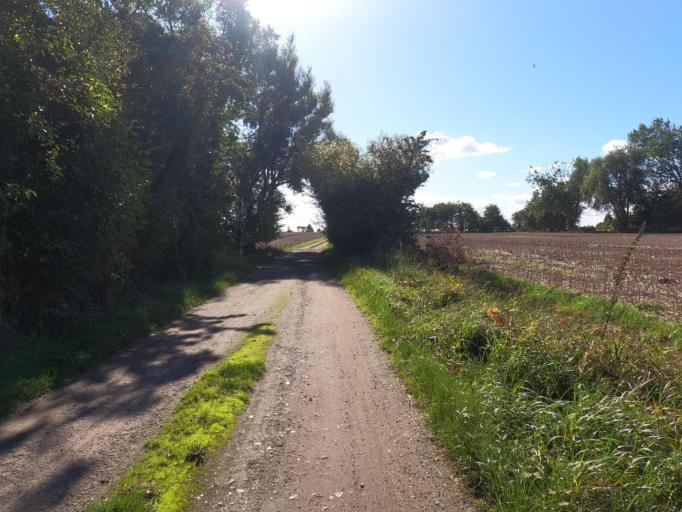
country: DE
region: Schleswig-Holstein
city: Grossenbrode
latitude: 54.3885
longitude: 11.1056
